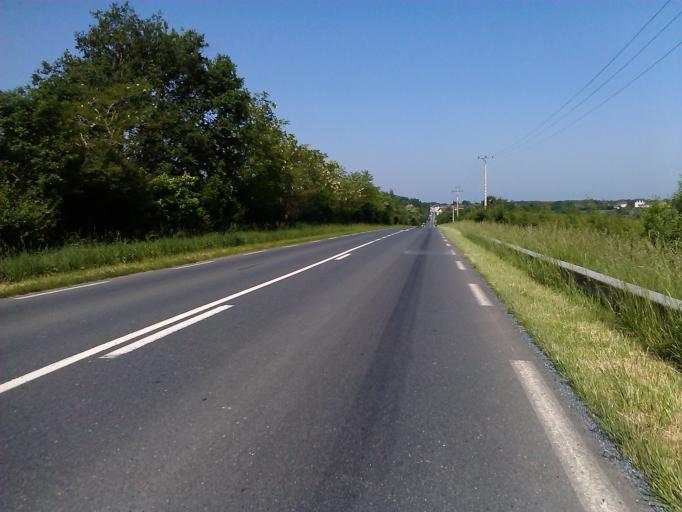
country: FR
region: Centre
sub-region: Departement de l'Indre
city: Arthon
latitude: 46.6112
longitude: 1.6983
